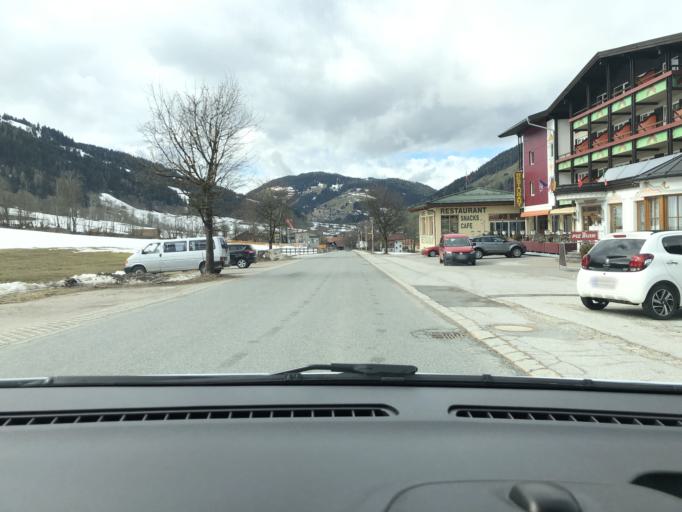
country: AT
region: Tyrol
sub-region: Politischer Bezirk Kitzbuhel
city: Itter
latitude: 47.4479
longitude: 12.1007
